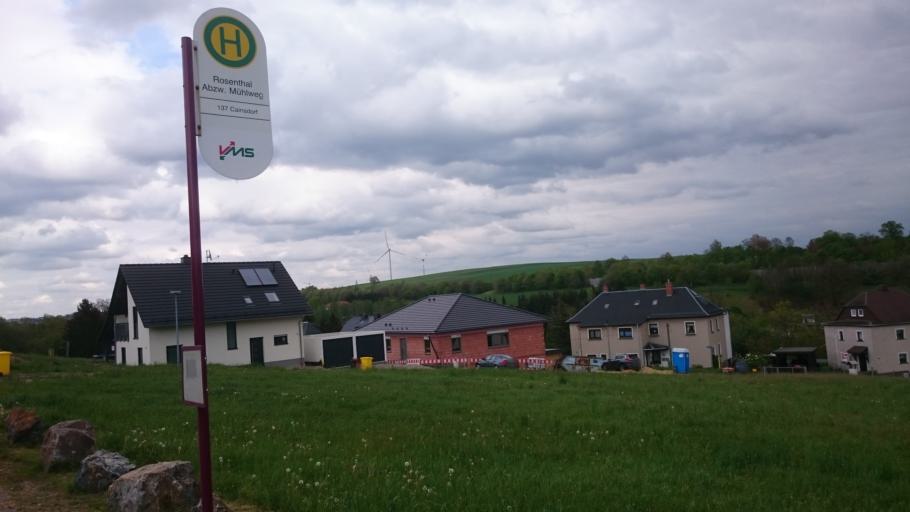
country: DE
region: Saxony
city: Wilkau-Hasslau
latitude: 50.6767
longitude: 12.5312
